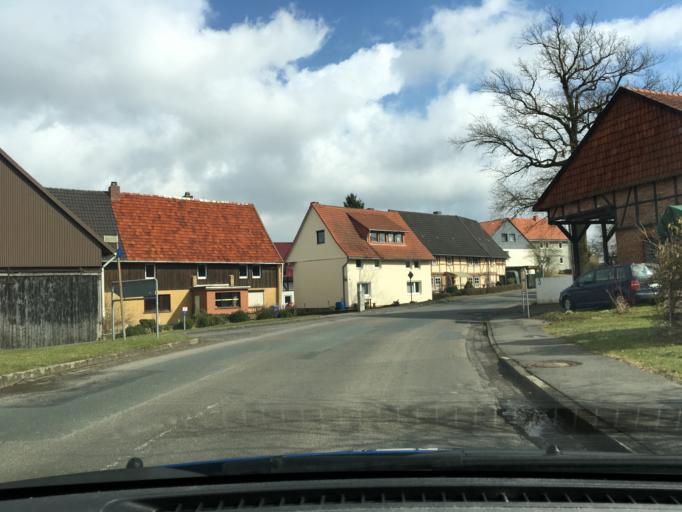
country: DE
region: Lower Saxony
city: Buhren
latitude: 51.5104
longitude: 9.6841
